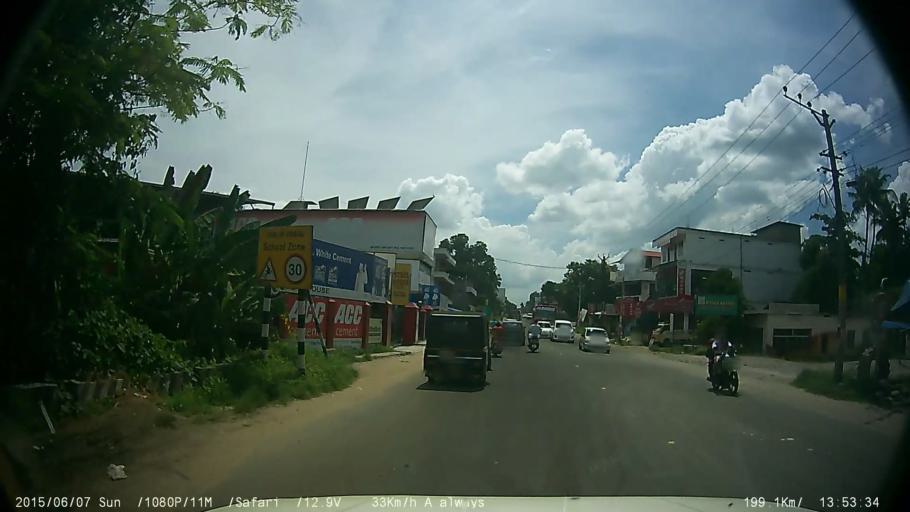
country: IN
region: Kerala
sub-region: Ernakulam
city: Angamali
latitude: 10.1682
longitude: 76.4345
